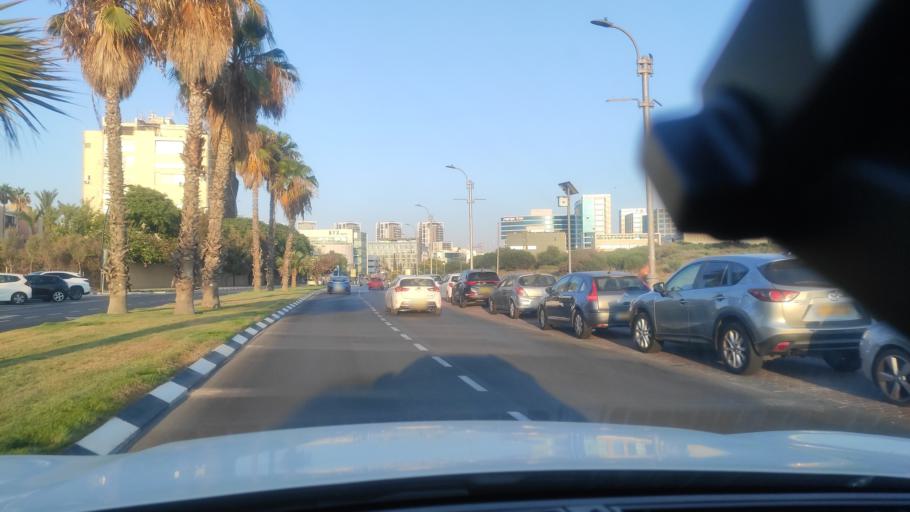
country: IL
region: Tel Aviv
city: Herzliya Pituah
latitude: 32.1638
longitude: 34.8033
